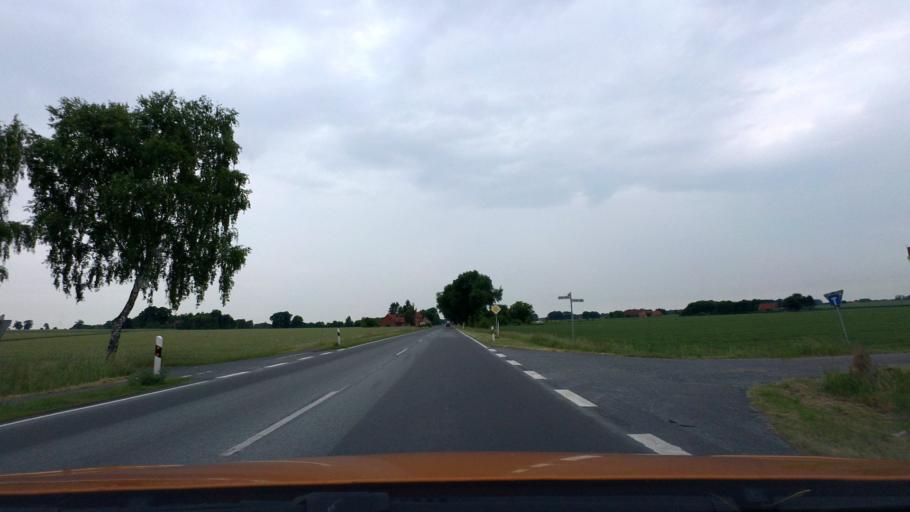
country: DE
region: Lower Saxony
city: Asendorf
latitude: 52.7464
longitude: 9.0215
